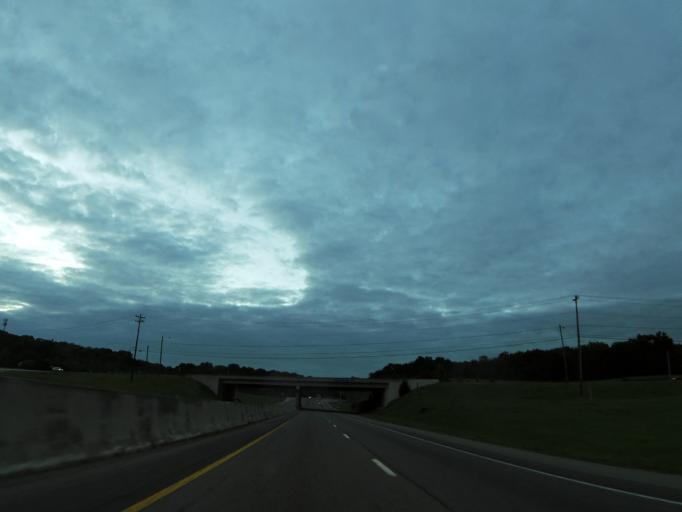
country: US
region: Tennessee
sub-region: Davidson County
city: Nashville
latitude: 36.2084
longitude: -86.8712
